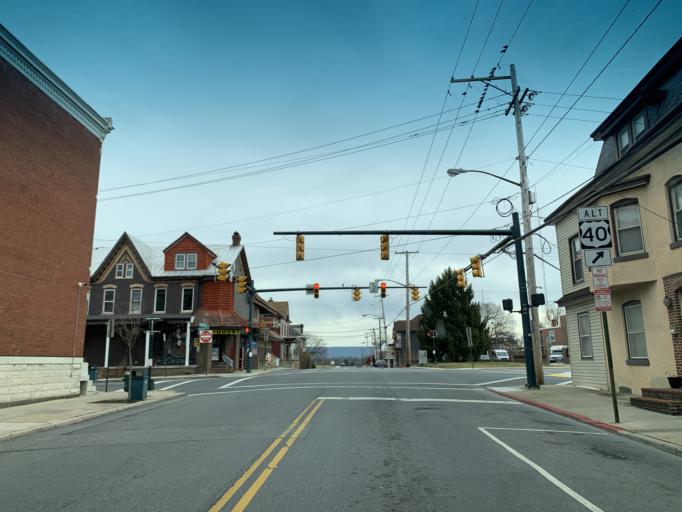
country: US
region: Maryland
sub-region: Washington County
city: Hagerstown
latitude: 39.6374
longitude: -77.7188
